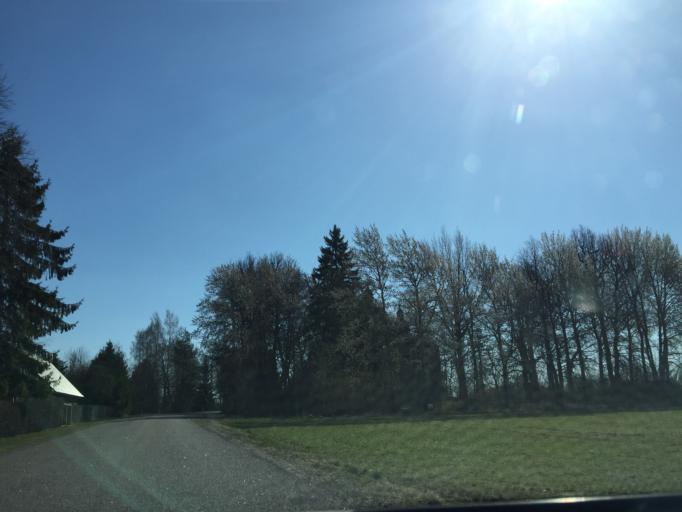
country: EE
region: Tartu
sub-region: Puhja vald
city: Puhja
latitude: 58.3415
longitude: 26.3572
